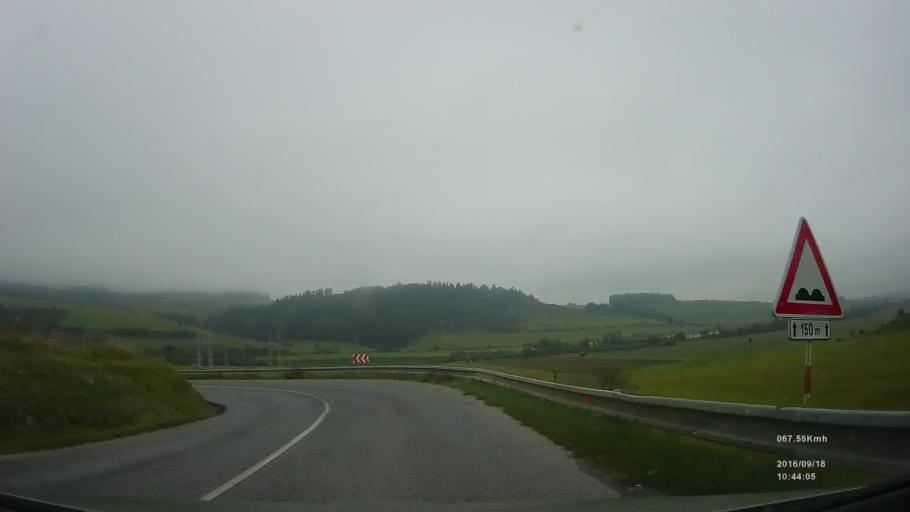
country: SK
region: Kosicky
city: Spisska Nova Ves
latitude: 48.9527
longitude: 20.5834
